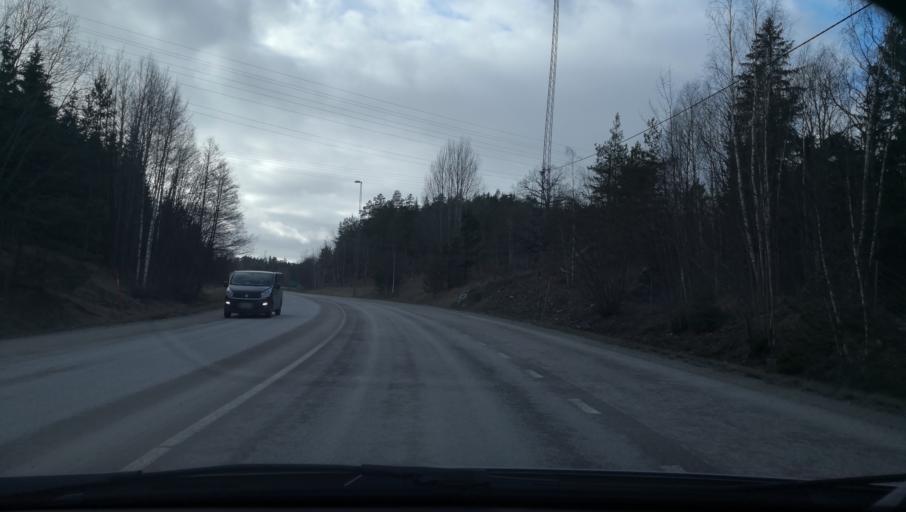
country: SE
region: Stockholm
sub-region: Varmdo Kommun
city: Gustavsberg
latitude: 59.3299
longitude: 18.3391
